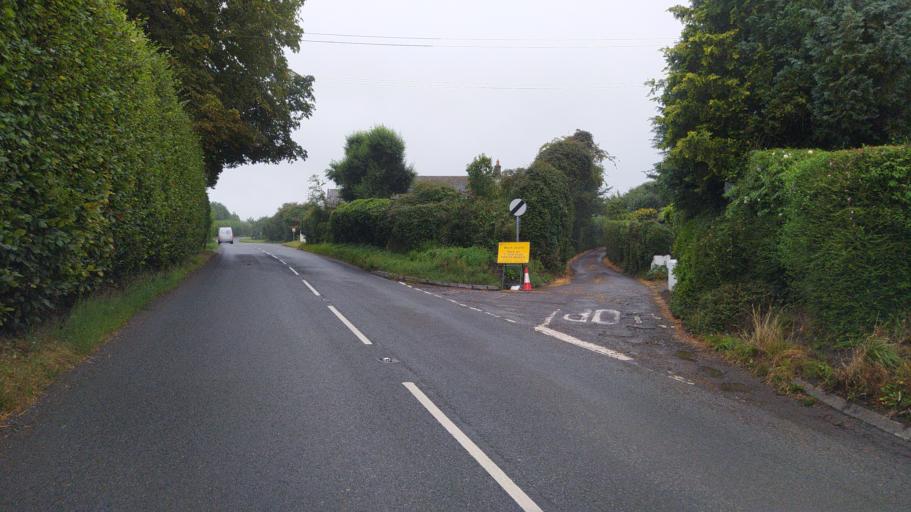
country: GB
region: England
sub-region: Wiltshire
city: Ansty
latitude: 51.0105
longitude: -2.1090
